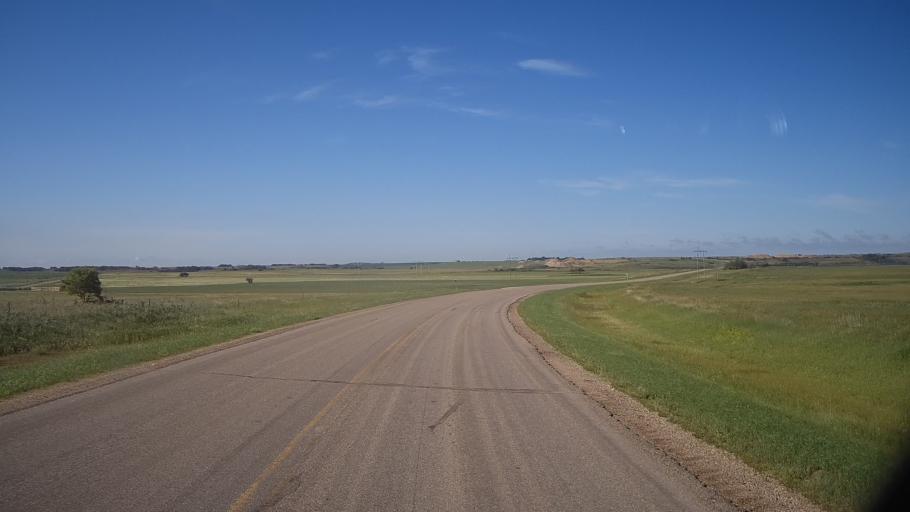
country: CA
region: Saskatchewan
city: Watrous
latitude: 51.7211
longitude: -105.3581
